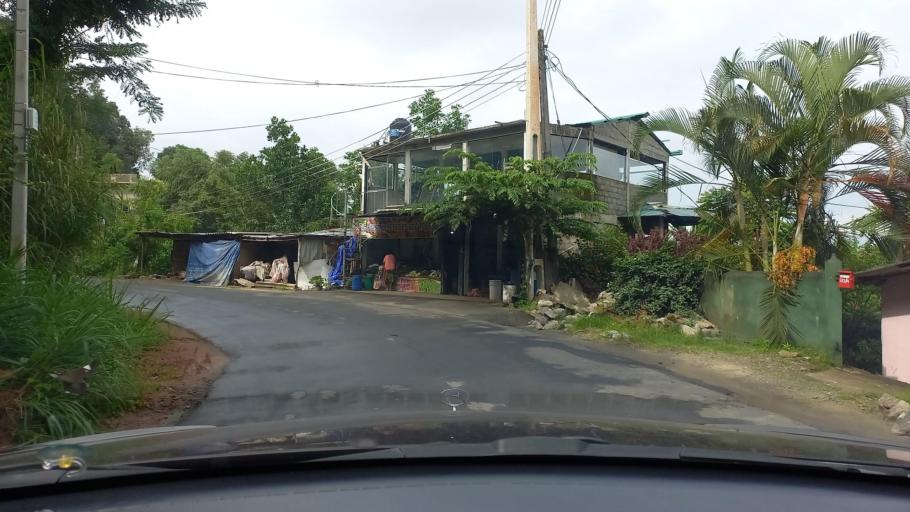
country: LK
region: Central
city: Gampola
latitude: 7.2160
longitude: 80.6143
